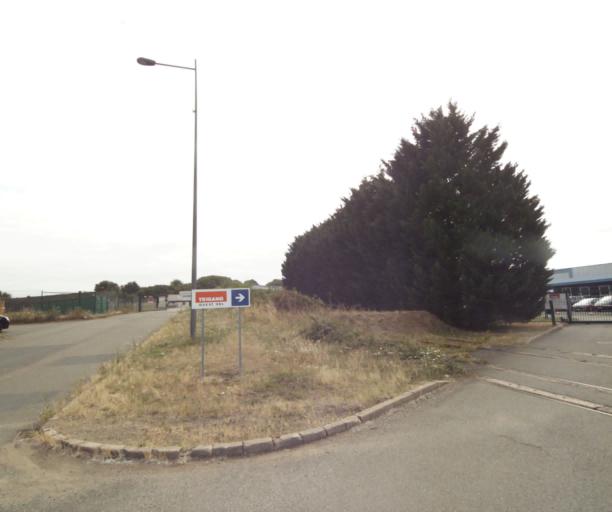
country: FR
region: Pays de la Loire
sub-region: Departement de la Sarthe
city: Solesmes
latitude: 47.8273
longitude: -0.3002
